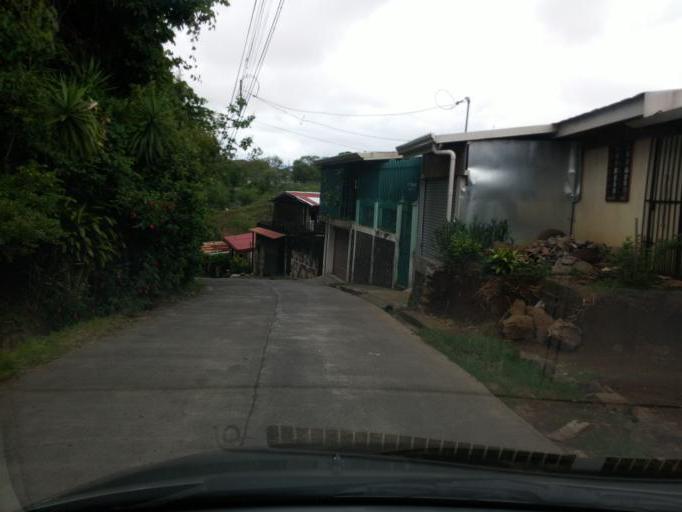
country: CR
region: Heredia
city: Mercedes
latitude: 10.0296
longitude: -84.1334
